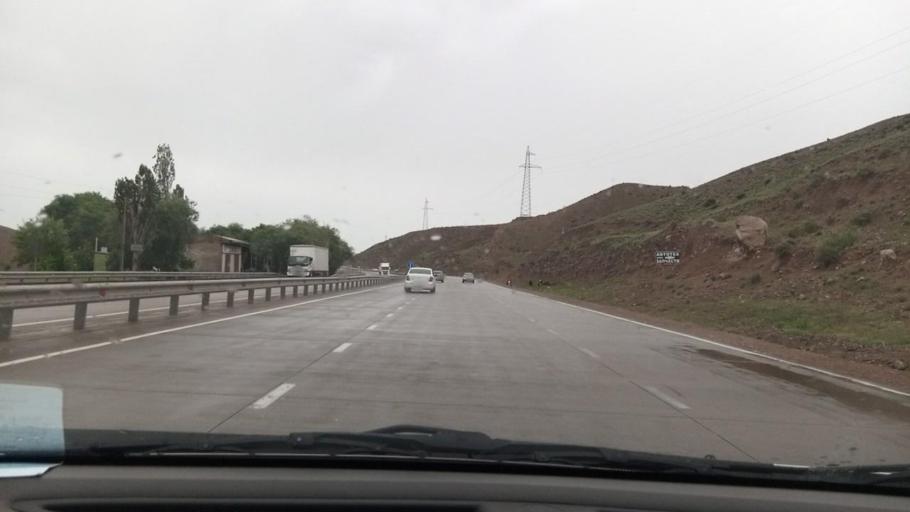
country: UZ
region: Namangan
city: Pop Shahri
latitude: 40.9478
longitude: 70.6813
